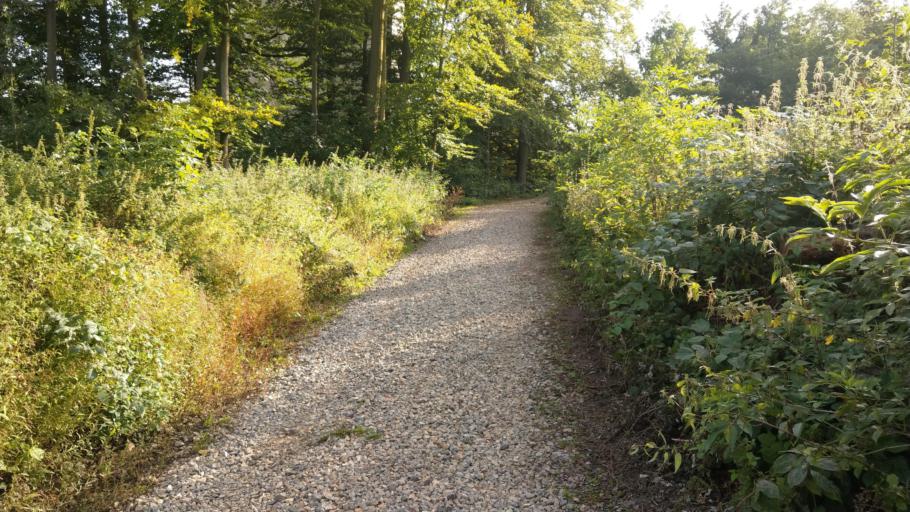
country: NL
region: Limburg
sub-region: Gemeente Vaals
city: Vaals
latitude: 50.7411
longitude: 6.0444
